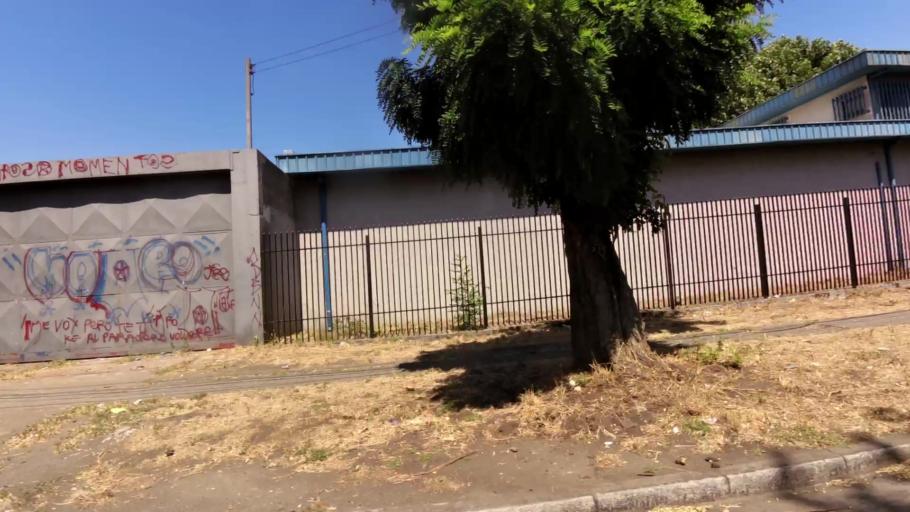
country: CL
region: Biobio
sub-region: Provincia de Concepcion
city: Concepcion
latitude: -36.8052
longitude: -73.0487
